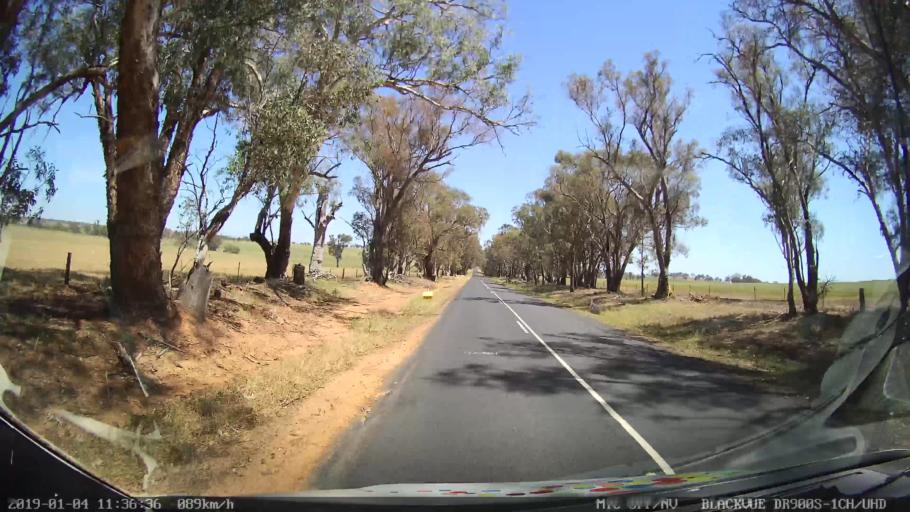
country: AU
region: New South Wales
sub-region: Cabonne
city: Molong
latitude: -33.0419
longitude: 148.8144
